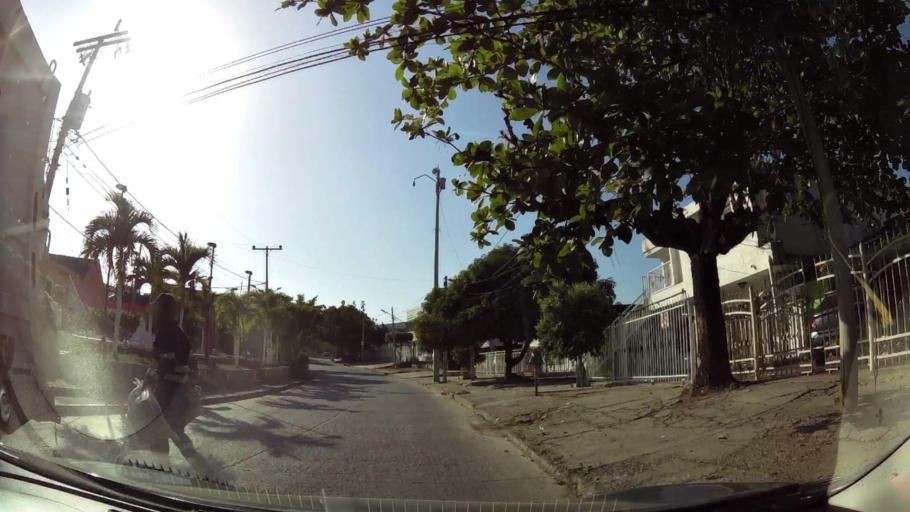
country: CO
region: Bolivar
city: Cartagena
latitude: 10.3836
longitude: -75.4843
